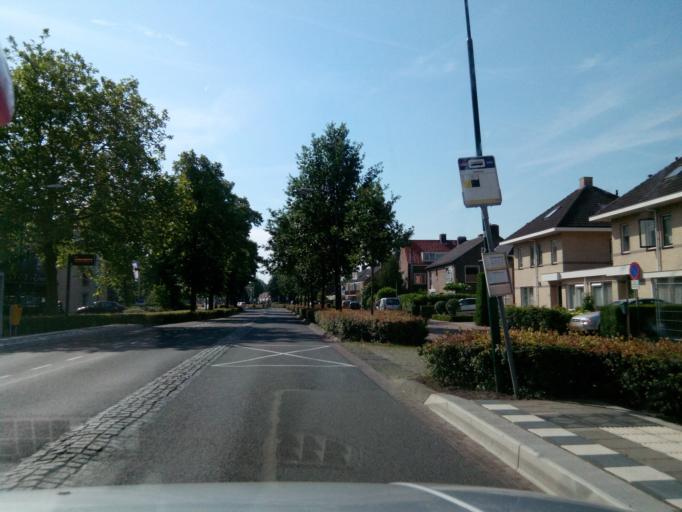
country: NL
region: Utrecht
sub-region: Gemeente Bunnik
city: Bunnik
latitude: 52.0665
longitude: 5.2022
